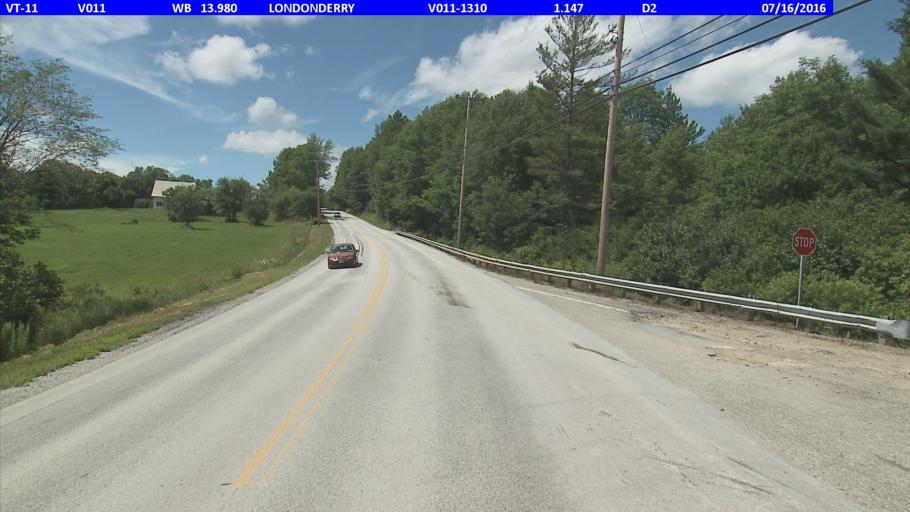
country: US
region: Vermont
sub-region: Windsor County
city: Chester
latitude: 43.2333
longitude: -72.8280
